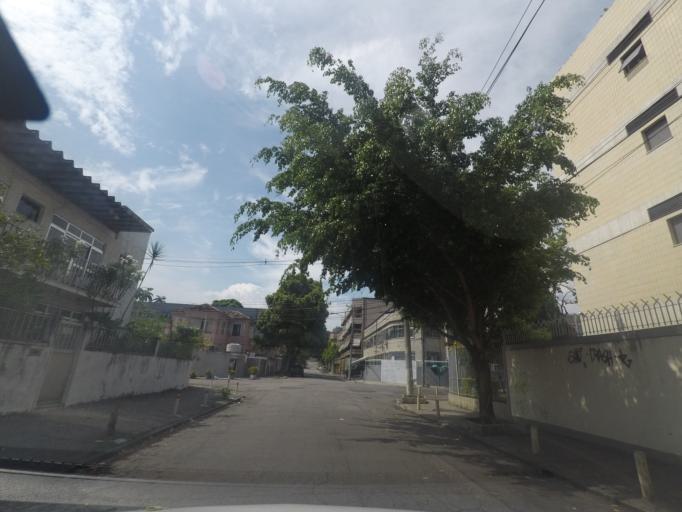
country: BR
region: Rio de Janeiro
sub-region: Rio De Janeiro
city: Rio de Janeiro
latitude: -22.8180
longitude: -43.2007
